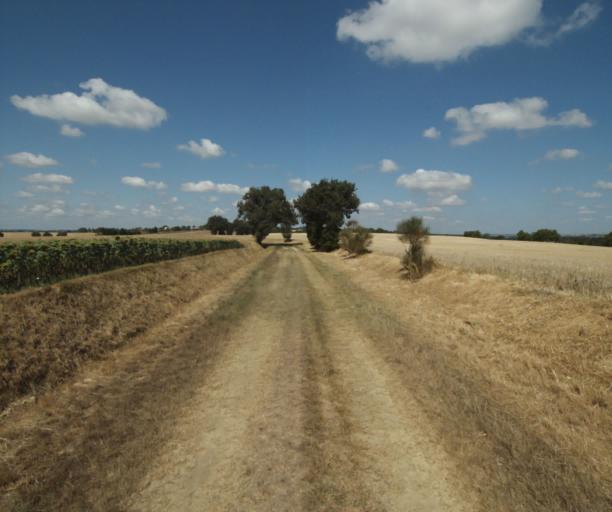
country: FR
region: Midi-Pyrenees
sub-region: Departement de la Haute-Garonne
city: Auriac-sur-Vendinelle
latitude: 43.4646
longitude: 1.8050
